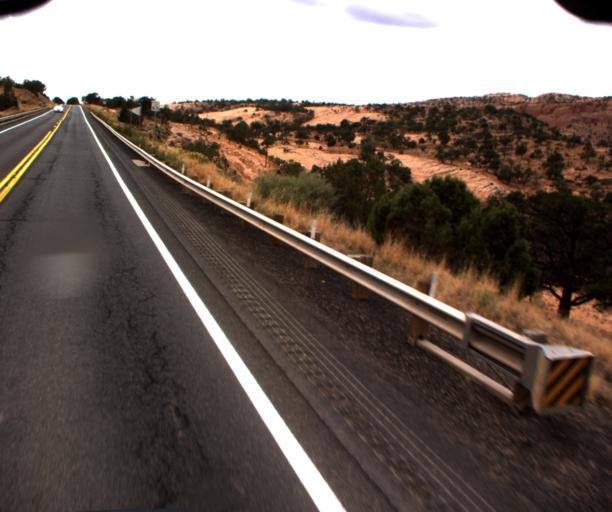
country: US
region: Arizona
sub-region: Navajo County
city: Kayenta
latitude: 36.6480
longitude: -110.4314
